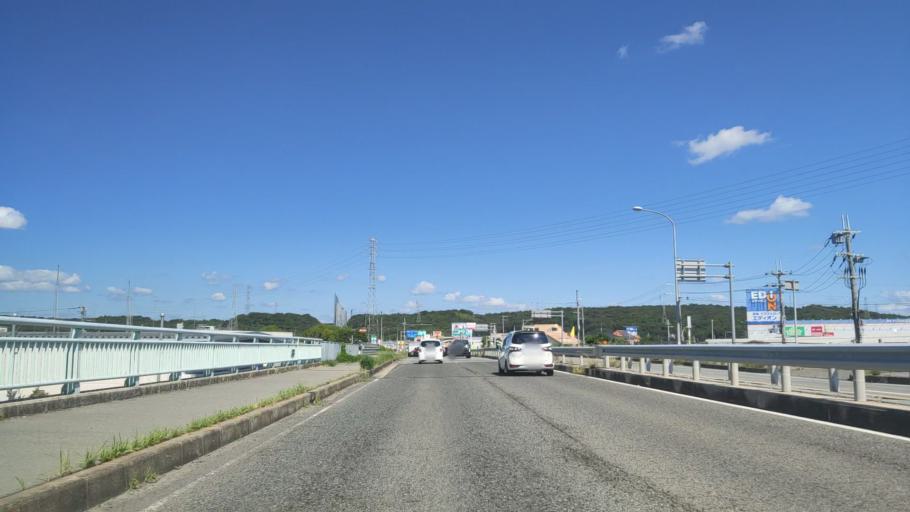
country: JP
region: Hyogo
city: Miki
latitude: 34.8014
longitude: 134.9659
